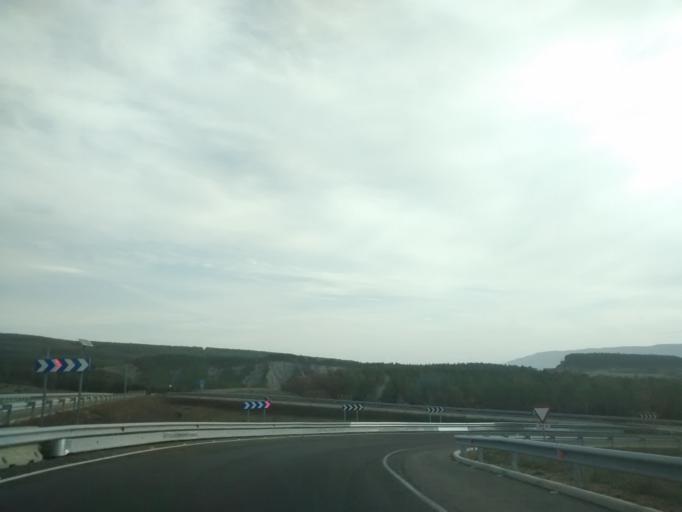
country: ES
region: Aragon
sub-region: Provincia de Zaragoza
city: Undues de Lerda
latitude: 42.6223
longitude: -1.1128
